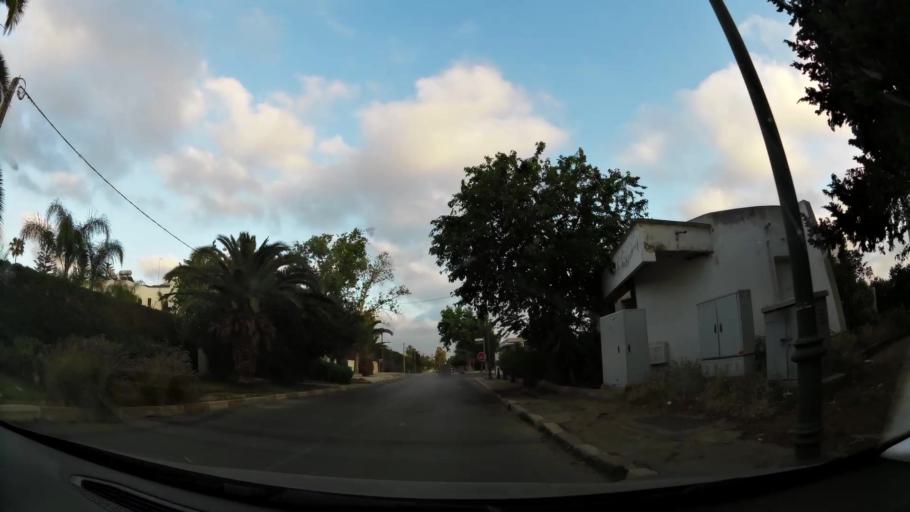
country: MA
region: Rabat-Sale-Zemmour-Zaer
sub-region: Rabat
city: Rabat
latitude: 33.9704
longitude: -6.8399
